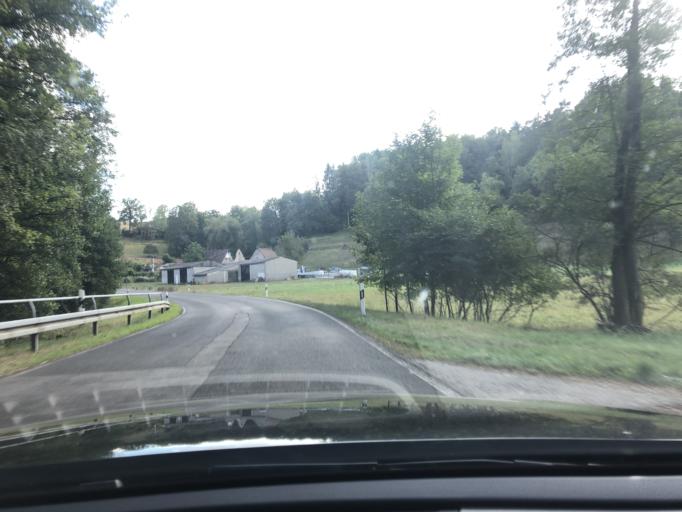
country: DE
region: Bavaria
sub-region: Regierungsbezirk Unterfranken
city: Breitbrunn
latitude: 50.0135
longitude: 10.6765
